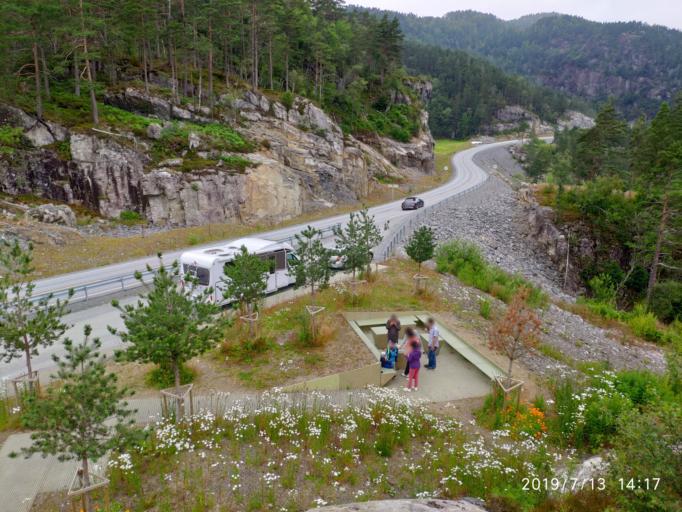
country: NO
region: Rogaland
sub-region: Suldal
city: Sand
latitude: 59.4135
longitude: 6.1172
